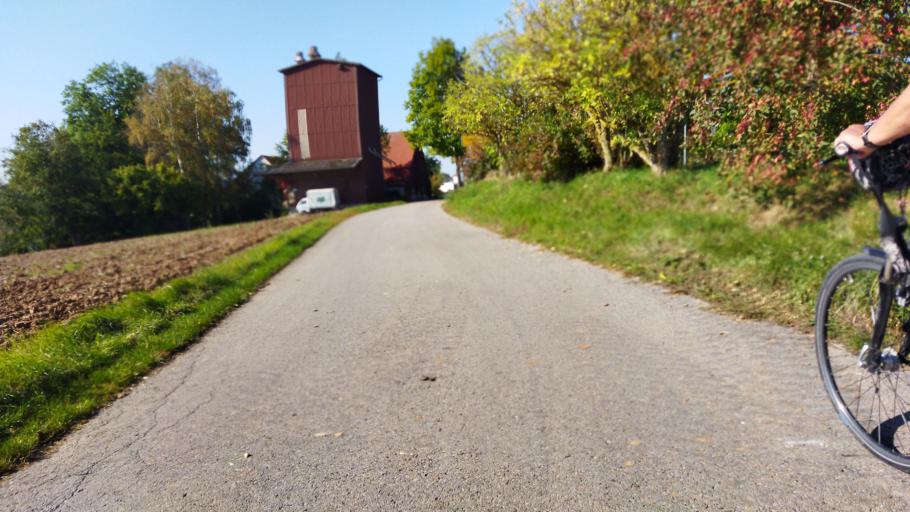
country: DE
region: Baden-Wuerttemberg
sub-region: Regierungsbezirk Stuttgart
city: Lochgau
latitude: 49.0149
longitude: 9.1088
